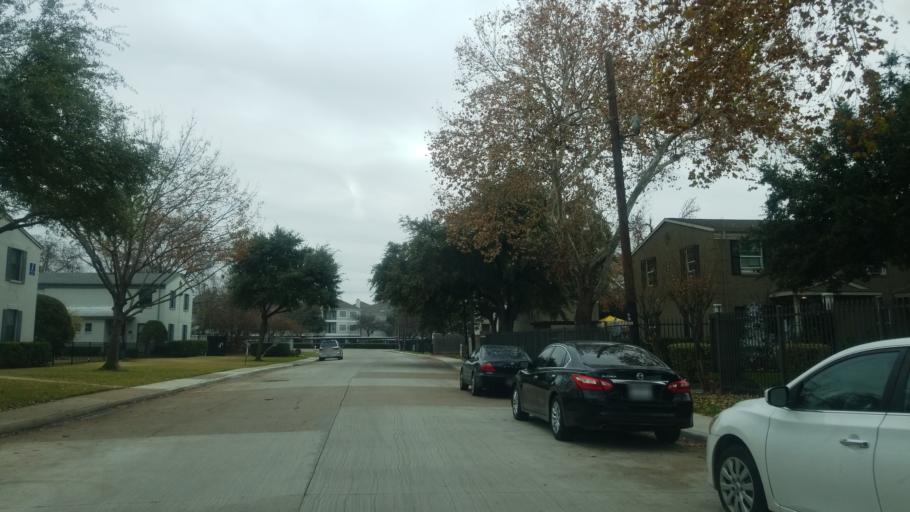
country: US
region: Texas
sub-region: Dallas County
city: Highland Park
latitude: 32.8214
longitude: -96.8205
